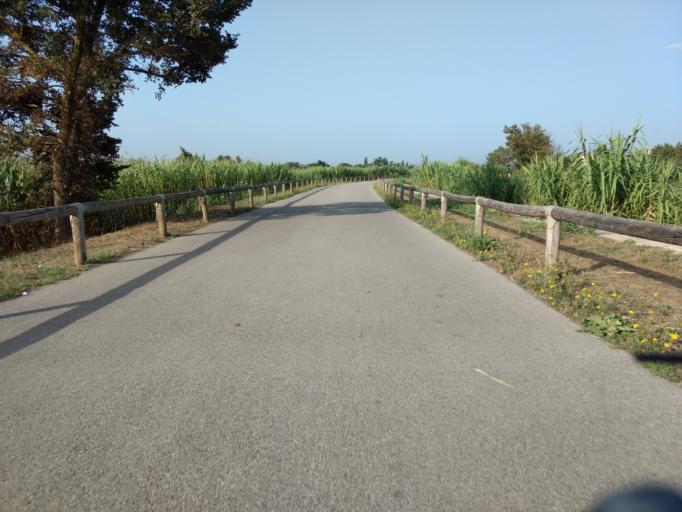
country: FR
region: Languedoc-Roussillon
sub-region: Departement des Pyrenees-Orientales
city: Le Barcares
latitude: 42.7723
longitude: 3.0260
